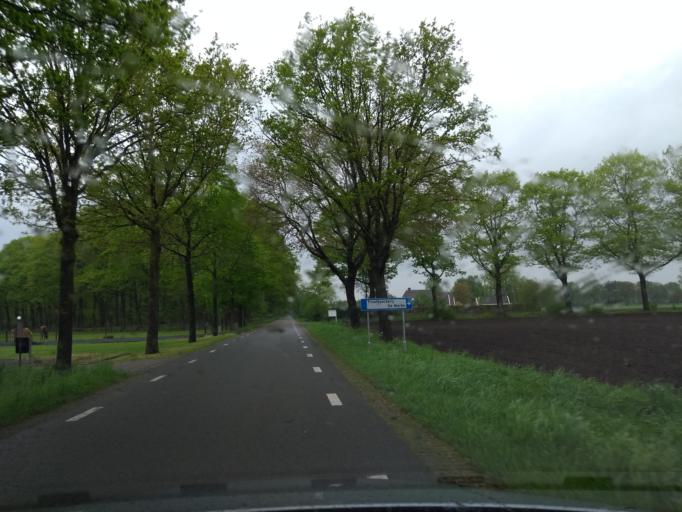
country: NL
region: Gelderland
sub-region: Gemeente Bronckhorst
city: Zelhem
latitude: 52.0362
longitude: 6.3406
